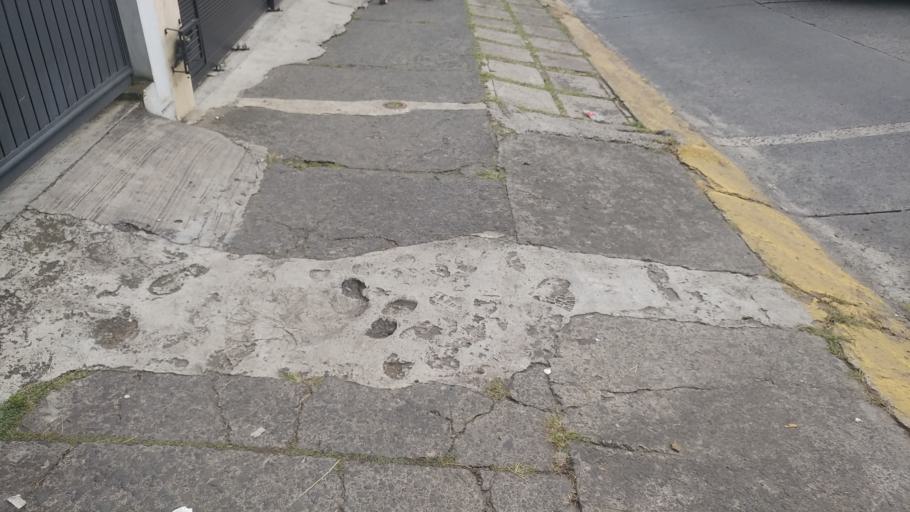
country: MX
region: Veracruz
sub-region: Xalapa
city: Xalapa de Enriquez
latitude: 19.5367
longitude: -96.9214
